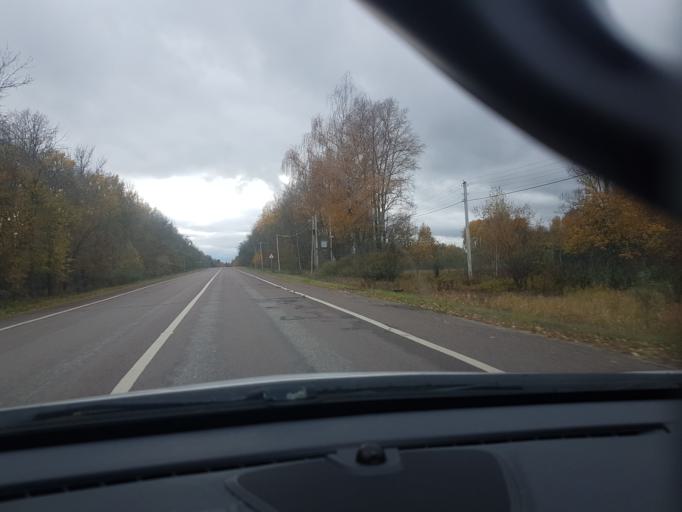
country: RU
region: Moskovskaya
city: Sychevo
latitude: 56.0071
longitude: 36.3360
